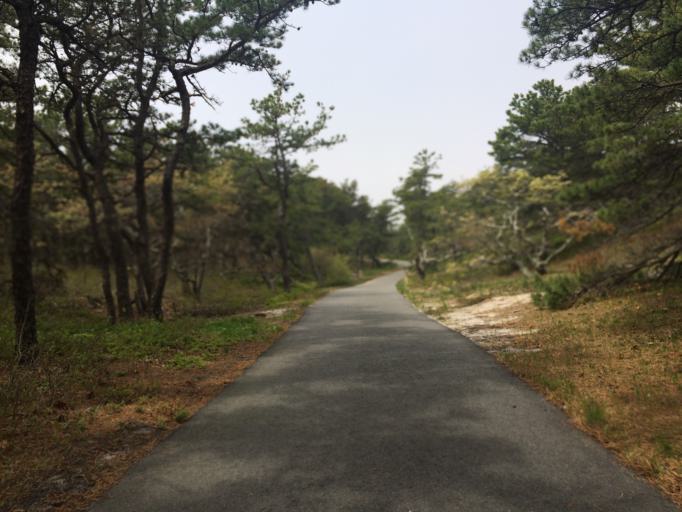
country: US
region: Massachusetts
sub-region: Barnstable County
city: Provincetown
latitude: 42.0762
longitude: -70.2107
